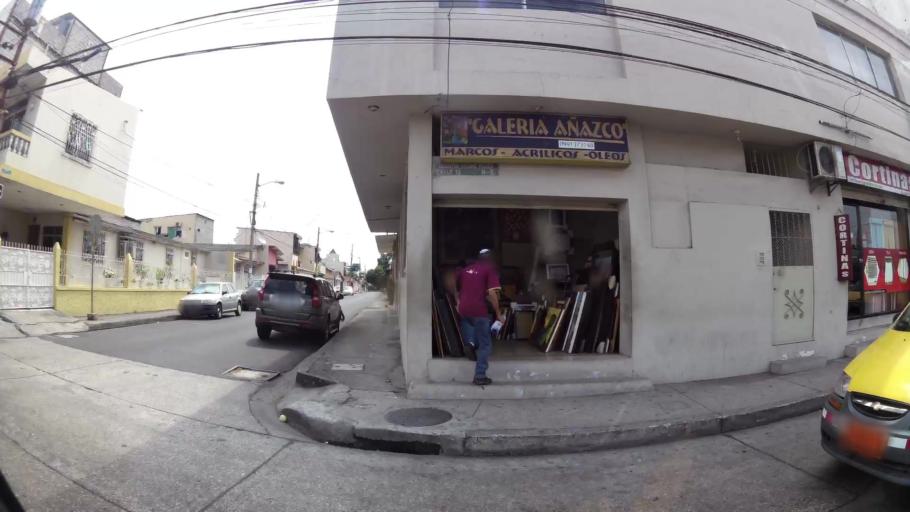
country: EC
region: Guayas
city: Eloy Alfaro
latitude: -2.1443
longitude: -79.8946
